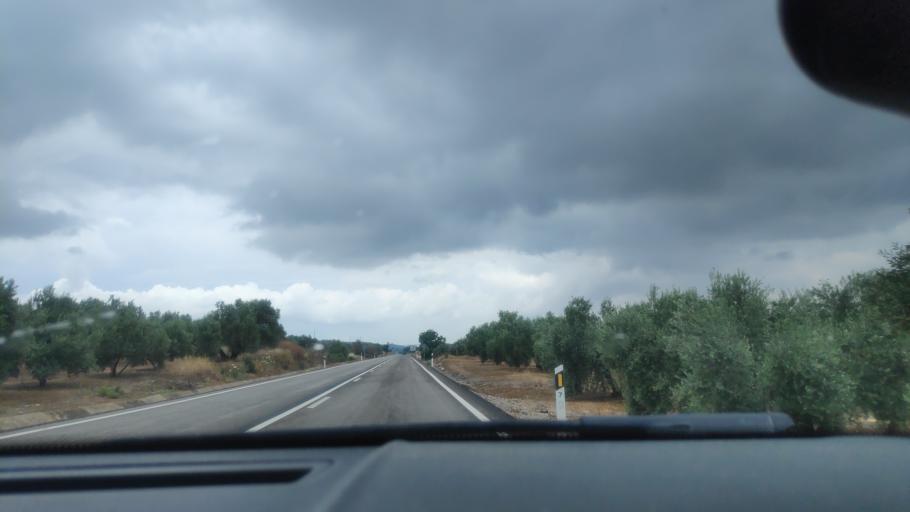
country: ES
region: Andalusia
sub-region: Provincia de Jaen
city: Jabalquinto
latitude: 38.0340
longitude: -3.7593
